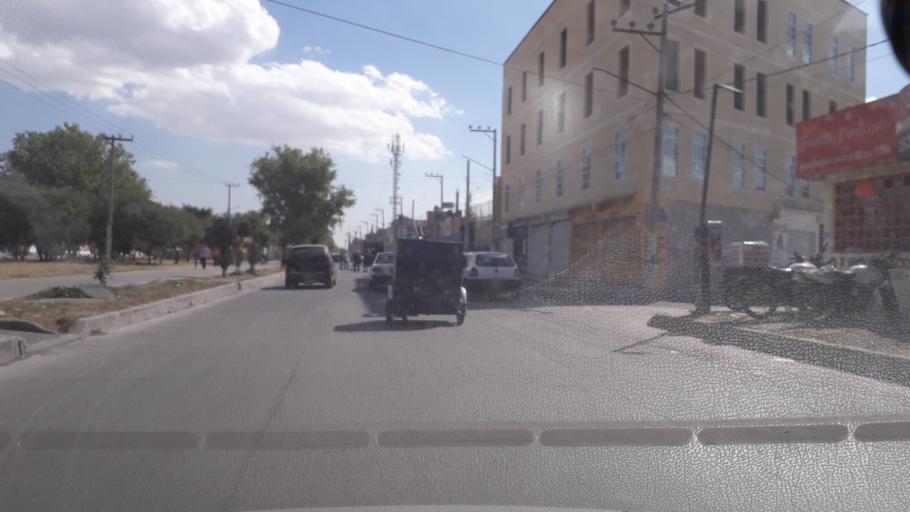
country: MX
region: Mexico
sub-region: Jaltenco
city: Alborada Jaltenco
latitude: 19.6571
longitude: -99.0686
